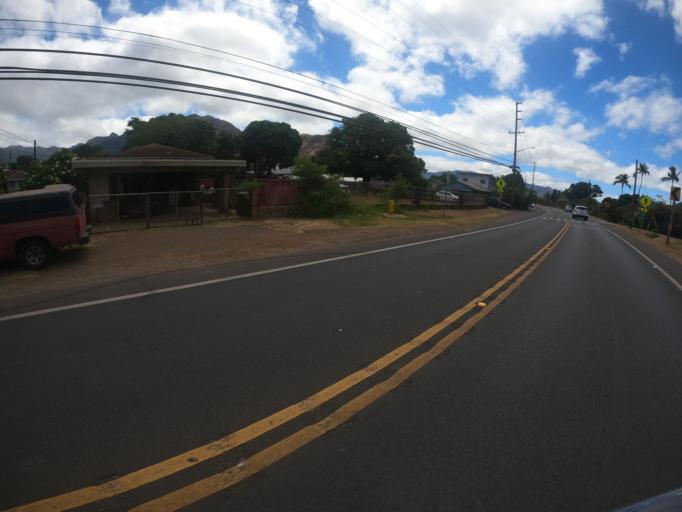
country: US
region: Hawaii
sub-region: Honolulu County
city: Makaha
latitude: 21.4633
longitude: -158.2118
